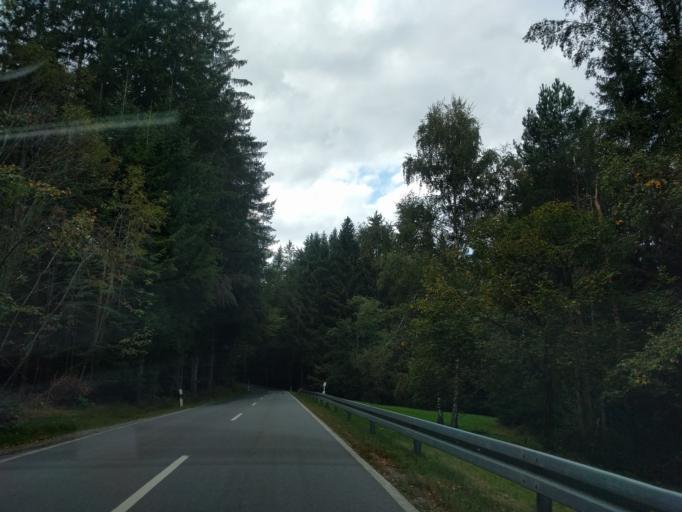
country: DE
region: Bavaria
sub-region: Lower Bavaria
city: Schaufling
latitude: 48.8722
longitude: 13.0379
